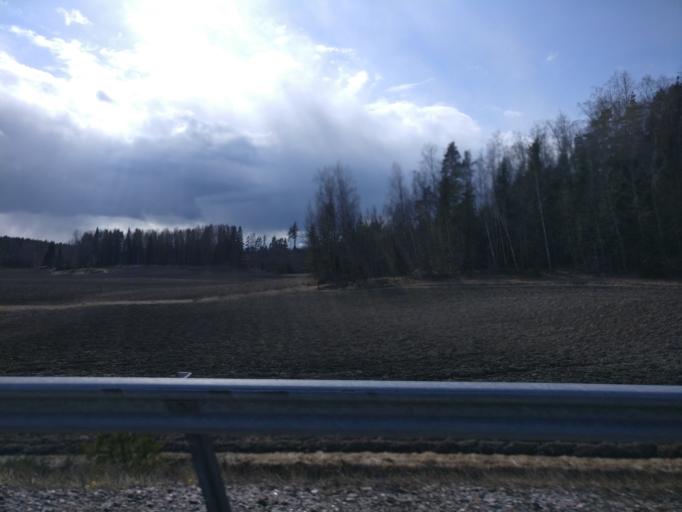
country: FI
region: Uusimaa
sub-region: Raaseporin
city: Inga
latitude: 60.0930
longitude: 23.9281
